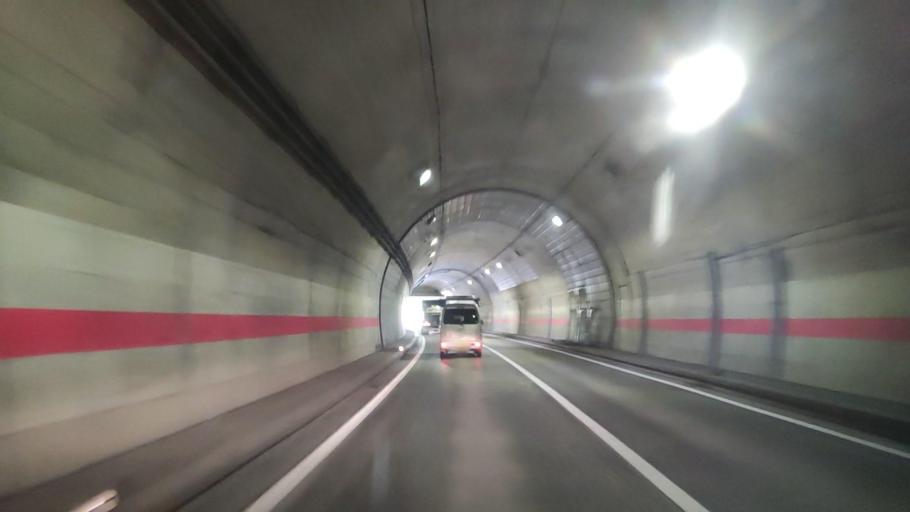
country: JP
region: Gifu
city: Takayama
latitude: 36.2564
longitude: 137.4730
